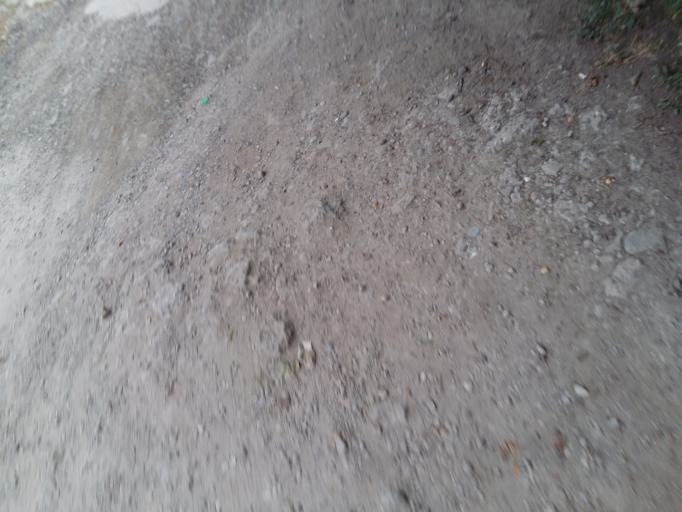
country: RU
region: Rostov
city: Imeni Chkalova
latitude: 47.2788
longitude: 39.7387
